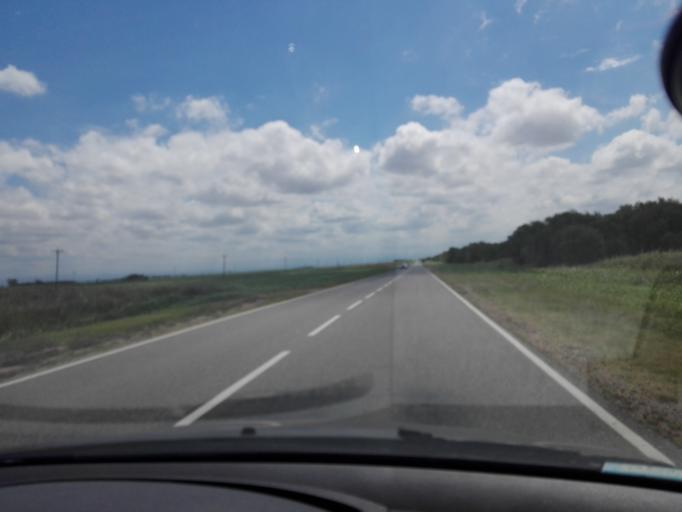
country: AR
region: Cordoba
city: Toledo
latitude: -31.6485
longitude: -64.1102
